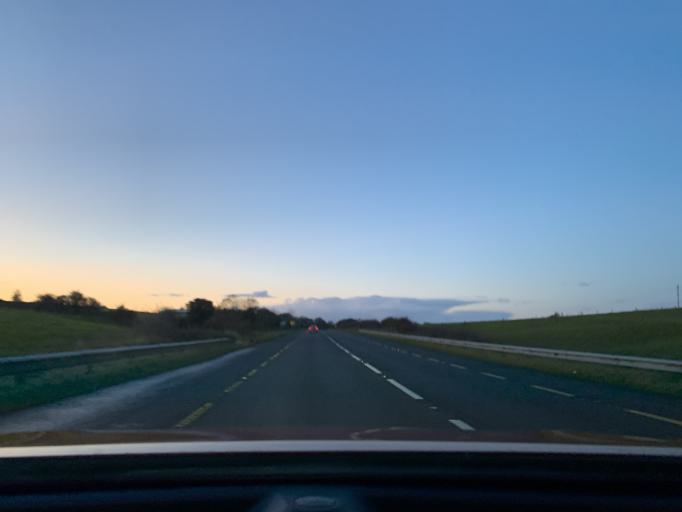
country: IE
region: Connaught
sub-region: County Leitrim
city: Carrick-on-Shannon
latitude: 53.9595
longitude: -8.1861
